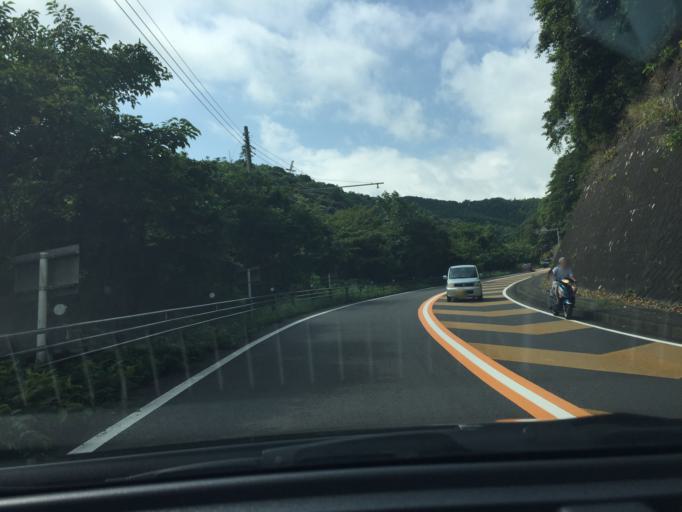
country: JP
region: Shizuoka
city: Ito
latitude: 34.9684
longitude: 139.1240
